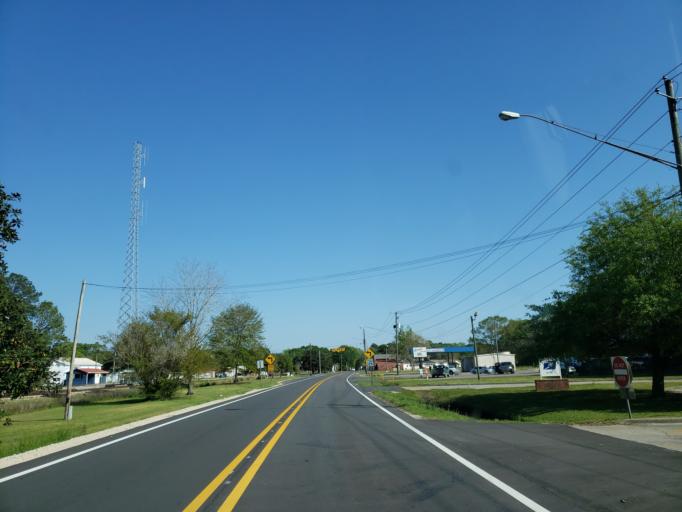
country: US
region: Mississippi
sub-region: Perry County
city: New Augusta
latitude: 31.1710
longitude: -88.9226
